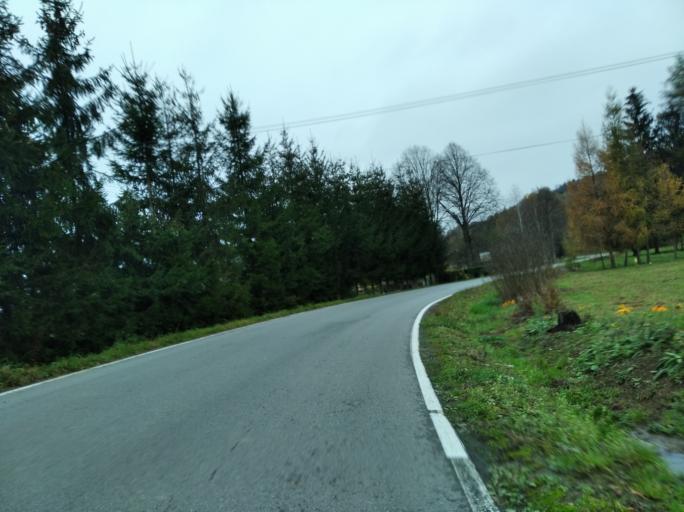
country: PL
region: Subcarpathian Voivodeship
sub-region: Powiat krosnienski
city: Leki
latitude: 49.8253
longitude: 21.6400
